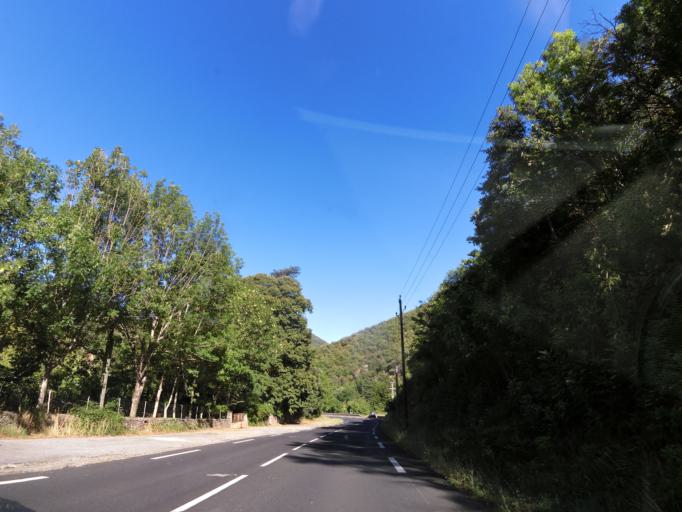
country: FR
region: Languedoc-Roussillon
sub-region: Departement du Gard
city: Valleraugue
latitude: 44.0775
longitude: 3.6588
